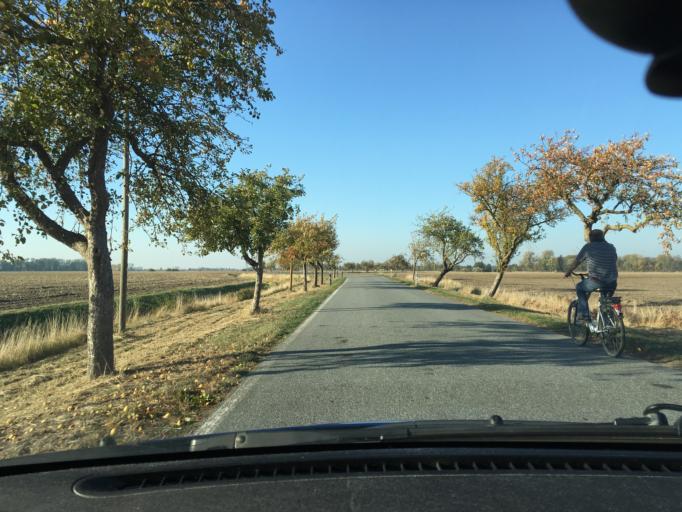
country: DE
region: Lower Saxony
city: Hitzacker
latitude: 53.1752
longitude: 11.0409
